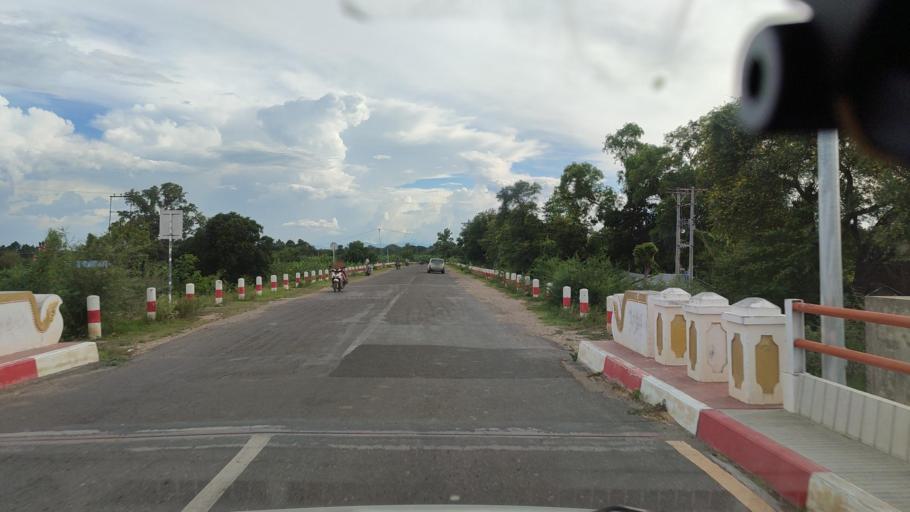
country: MM
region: Magway
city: Yenangyaung
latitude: 20.3866
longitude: 94.6855
